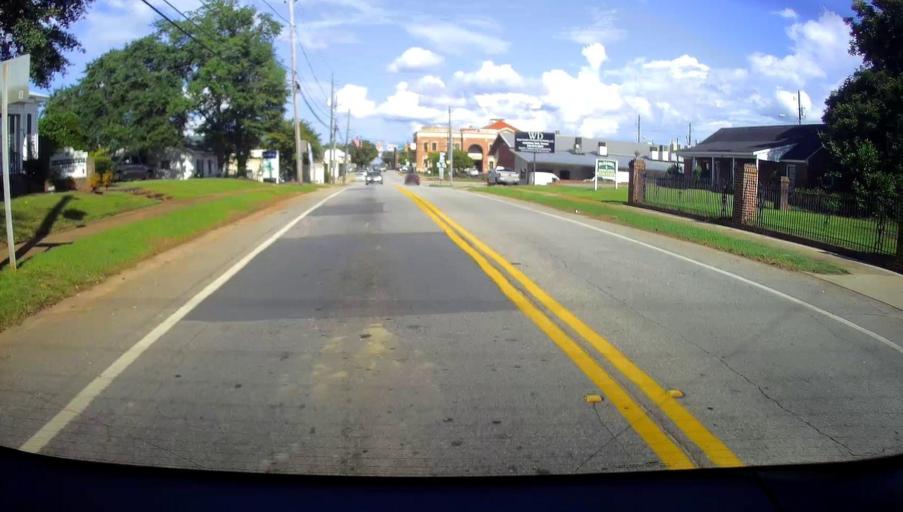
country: US
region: Georgia
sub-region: Upson County
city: Thomaston
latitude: 32.8880
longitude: -84.3290
